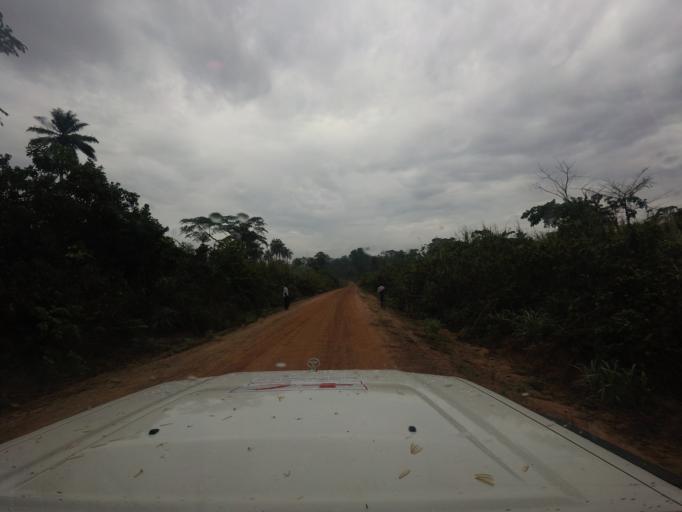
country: LR
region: Lofa
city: Voinjama
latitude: 8.3932
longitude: -9.8065
